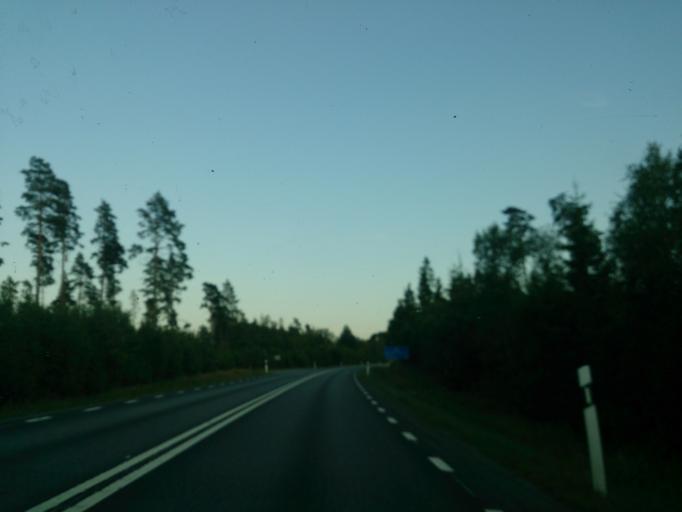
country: SE
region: Joenkoeping
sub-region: Varnamo Kommun
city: Rydaholm
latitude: 57.0297
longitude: 14.2547
